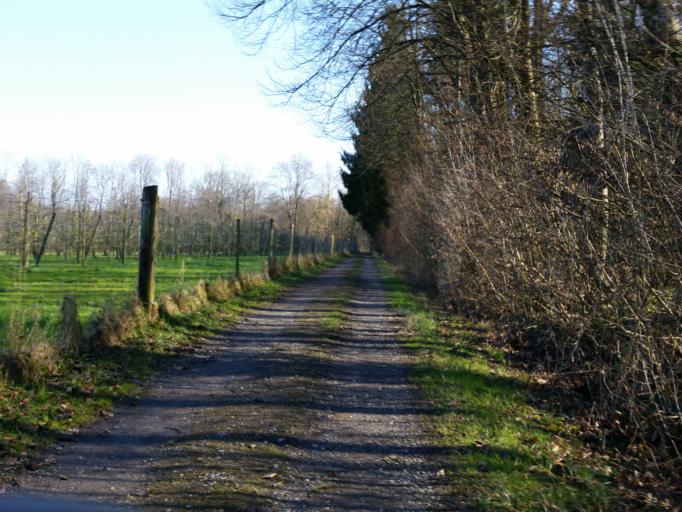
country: CH
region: Thurgau
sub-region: Arbon District
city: Uttwil
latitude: 47.5724
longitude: 9.3454
